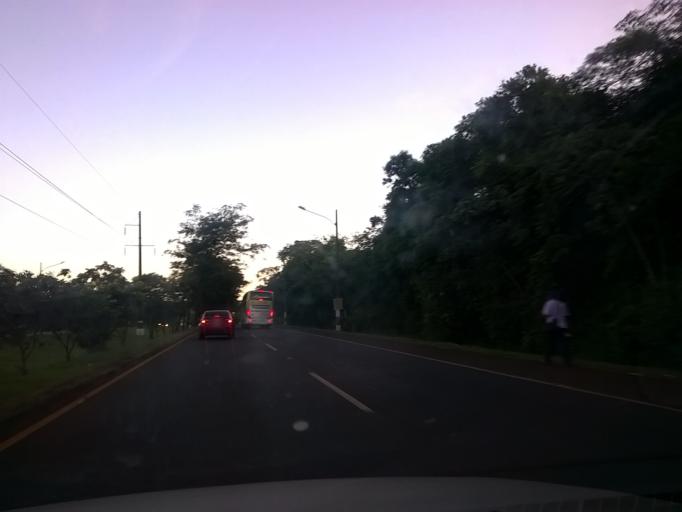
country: PY
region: Alto Parana
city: Ciudad del Este
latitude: -25.4798
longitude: -54.6259
